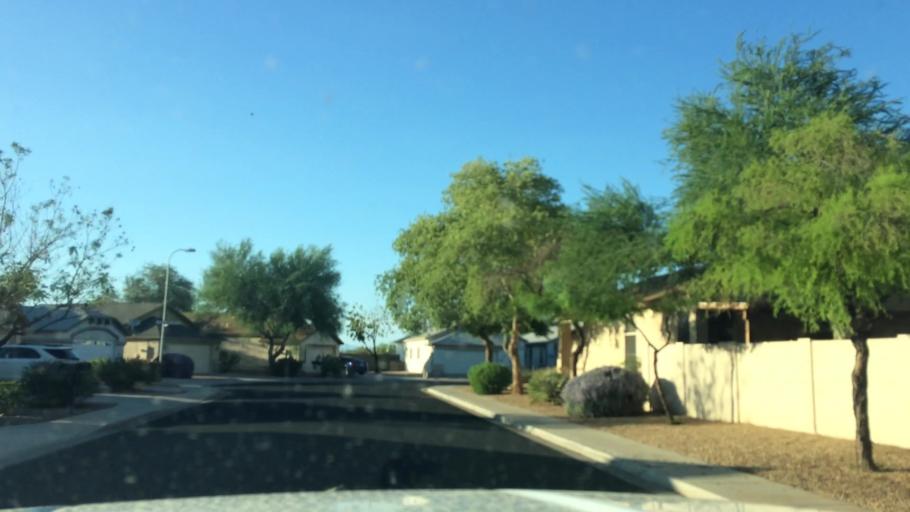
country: US
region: Arizona
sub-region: Maricopa County
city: Sun City
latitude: 33.5723
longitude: -112.2704
